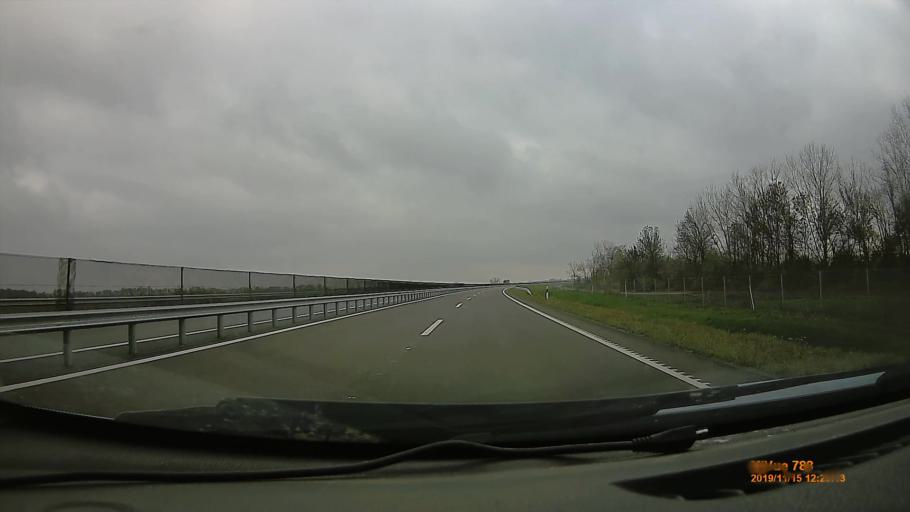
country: HU
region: Bekes
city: Kondoros
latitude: 46.7686
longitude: 20.7455
